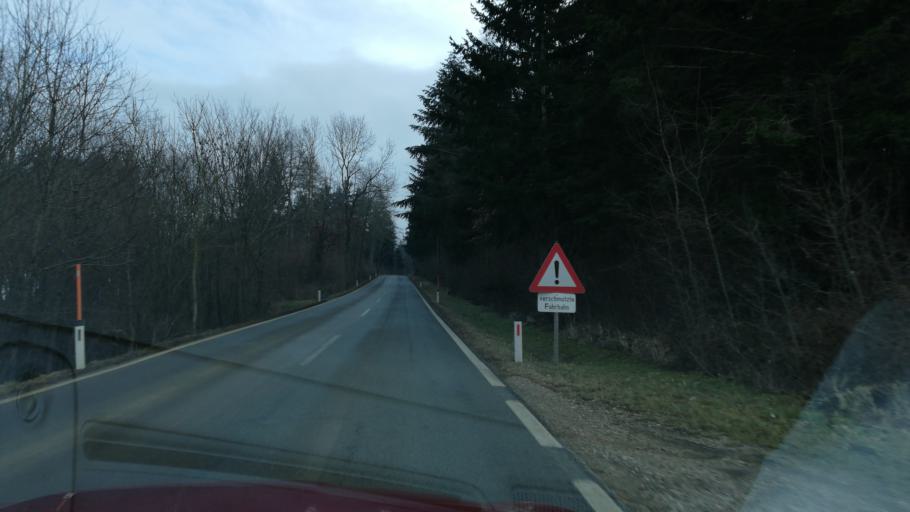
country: AT
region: Upper Austria
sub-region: Politischer Bezirk Vocklabruck
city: Wolfsegg am Hausruck
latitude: 48.1864
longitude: 13.7136
